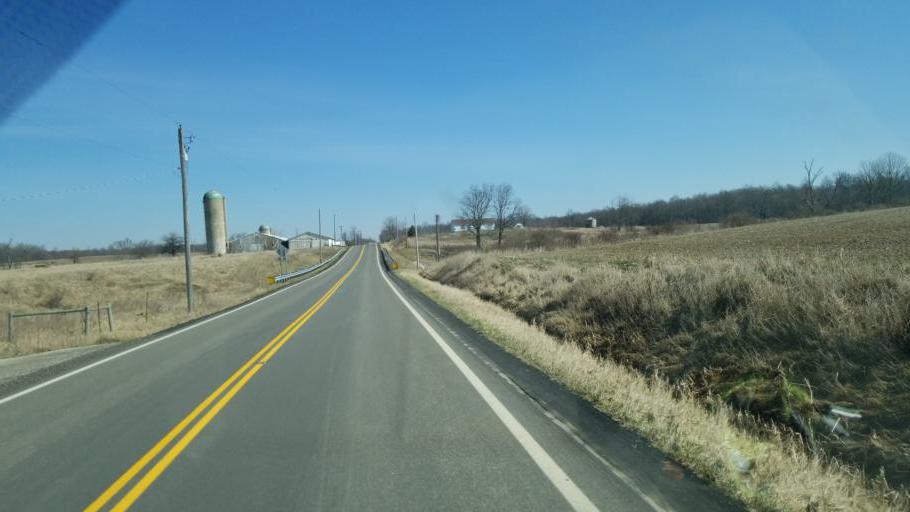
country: US
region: Ohio
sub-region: Wayne County
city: West Salem
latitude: 40.9756
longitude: -82.2402
